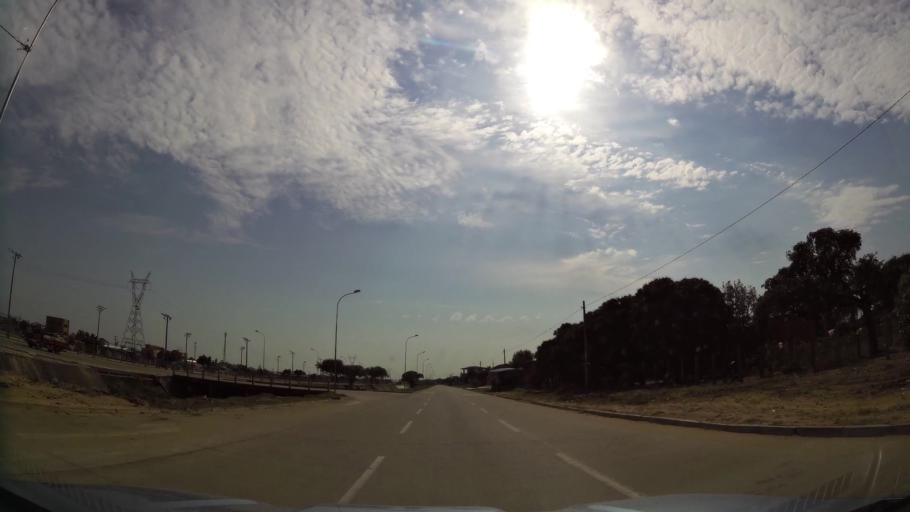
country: BO
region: Santa Cruz
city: Santa Cruz de la Sierra
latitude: -17.7316
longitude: -63.1378
